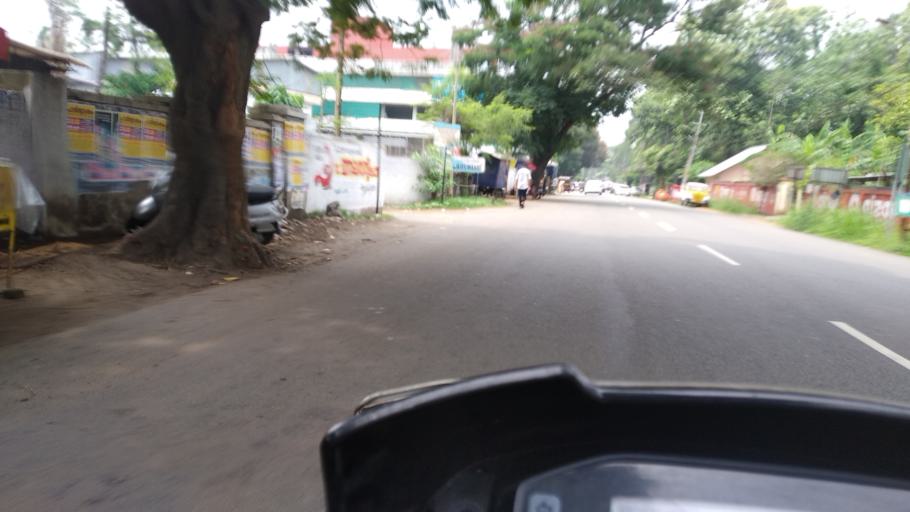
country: IN
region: Kerala
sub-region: Ernakulam
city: Perumpavur
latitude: 10.1158
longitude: 76.4825
